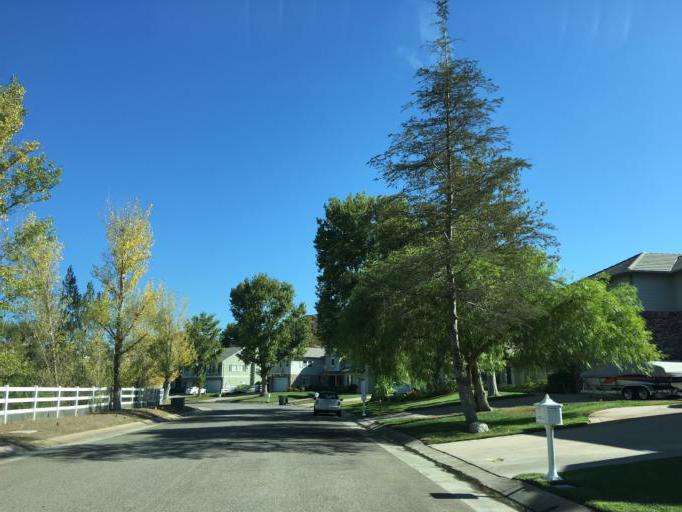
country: US
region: California
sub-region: Los Angeles County
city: Agua Dulce
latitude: 34.3997
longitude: -118.4017
